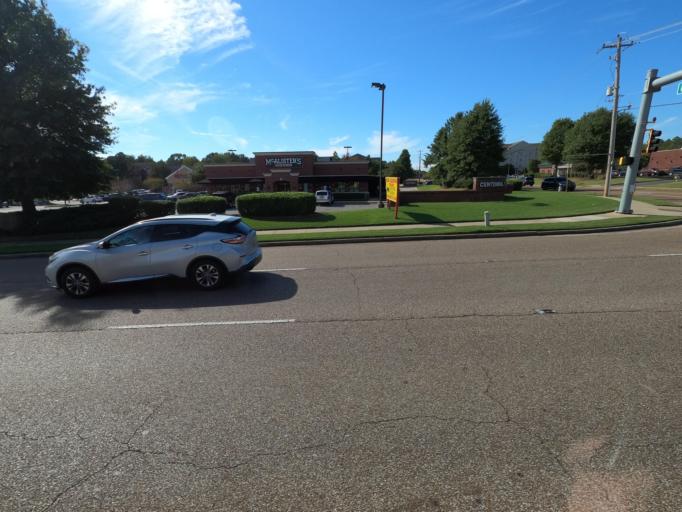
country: US
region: Tennessee
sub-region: Shelby County
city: Germantown
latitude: 35.0435
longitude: -89.7960
